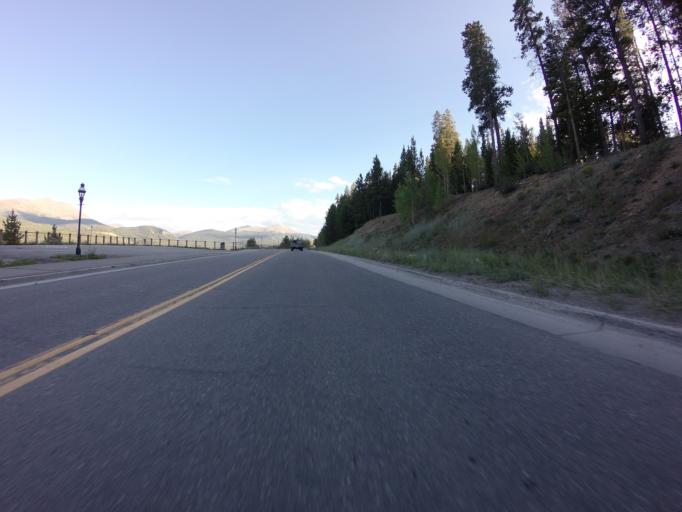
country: US
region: Colorado
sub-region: Summit County
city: Breckenridge
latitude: 39.4866
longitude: -106.0525
